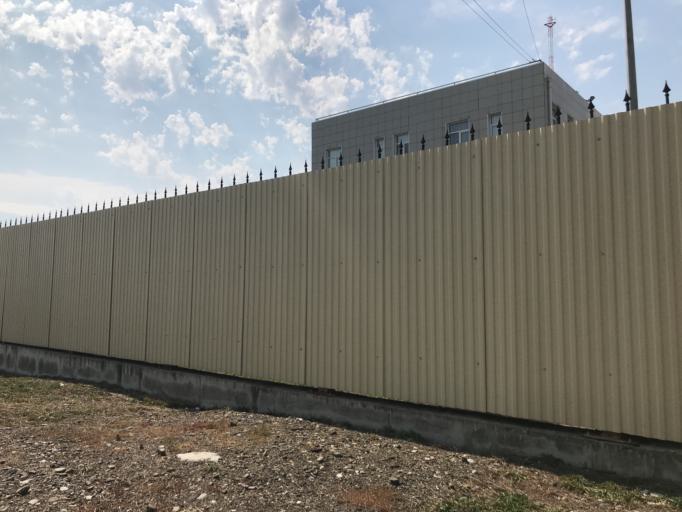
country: RU
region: Krasnodarskiy
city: Vysokoye
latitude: 43.3999
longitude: 39.9844
